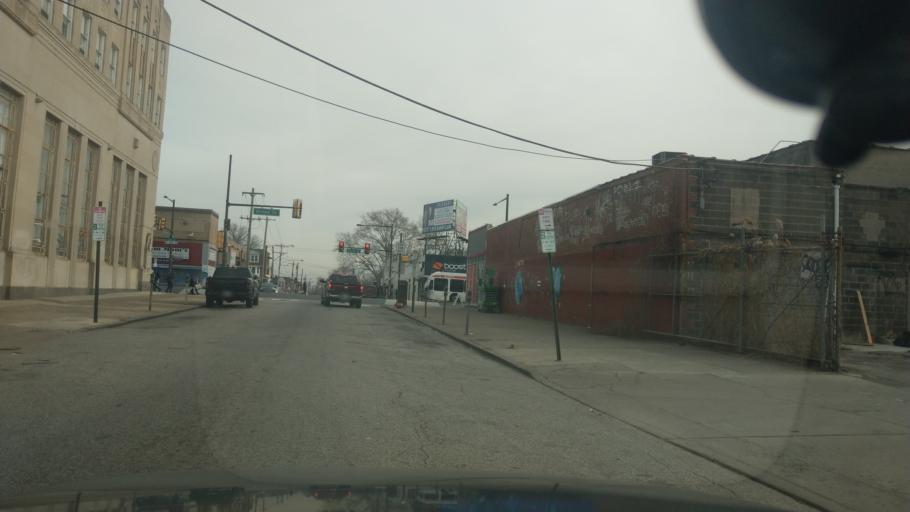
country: US
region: Pennsylvania
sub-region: Montgomery County
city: Wyncote
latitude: 40.0399
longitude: -75.1453
